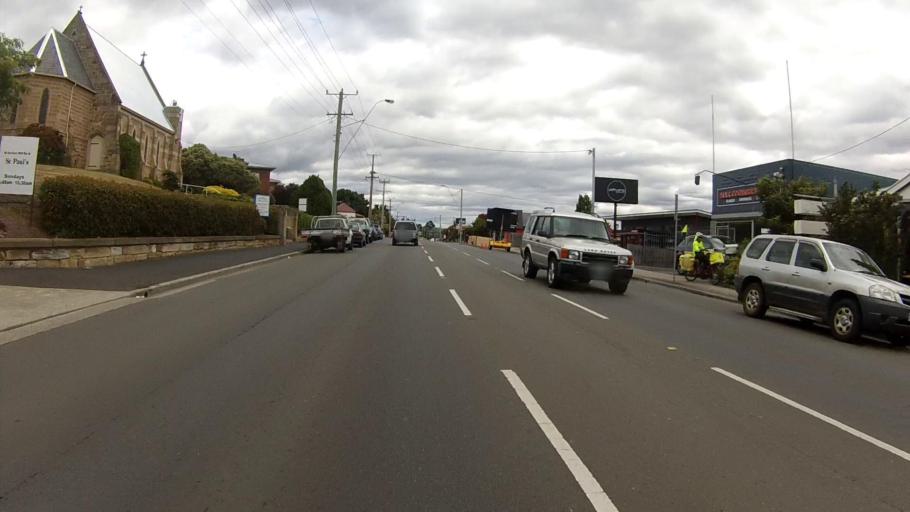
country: AU
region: Tasmania
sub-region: Glenorchy
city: Glenorchy
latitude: -42.8275
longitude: 147.2675
